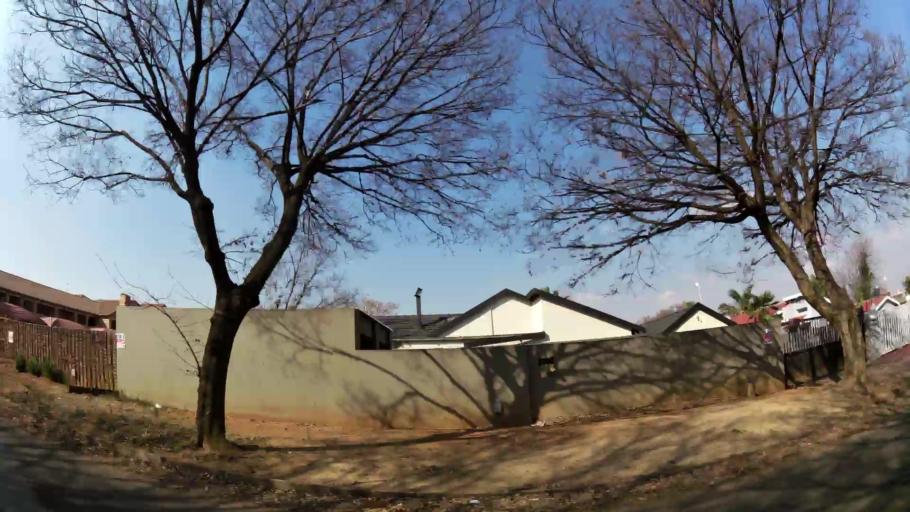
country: ZA
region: Gauteng
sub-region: Ekurhuleni Metropolitan Municipality
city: Boksburg
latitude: -26.1874
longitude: 28.2660
